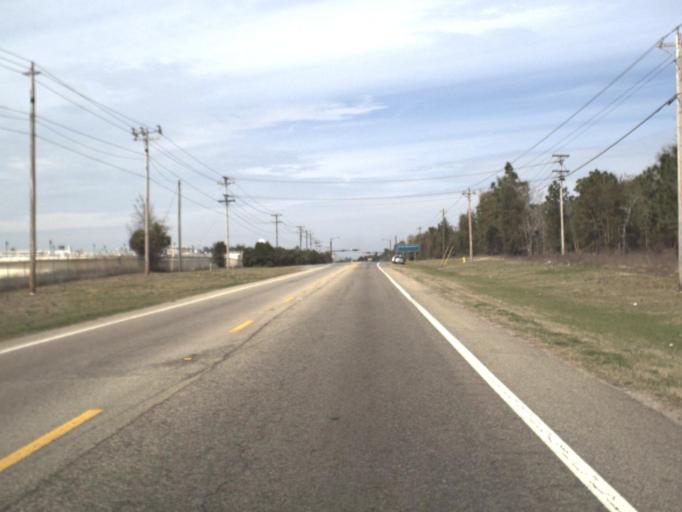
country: US
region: Florida
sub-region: Leon County
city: Tallahassee
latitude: 30.3913
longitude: -84.3183
